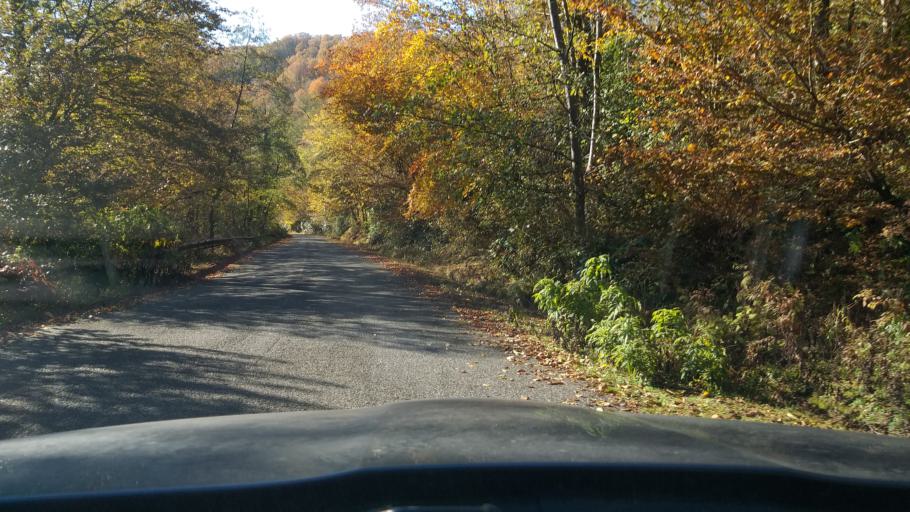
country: GE
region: Abkhazia
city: Bich'vinta
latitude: 43.1909
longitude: 40.4552
